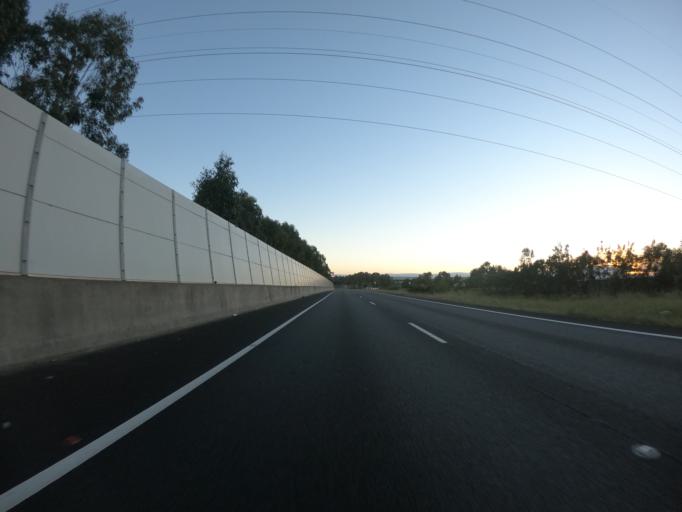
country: AU
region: New South Wales
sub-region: Blacktown
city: Glendenning
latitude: -33.7600
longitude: 150.8470
